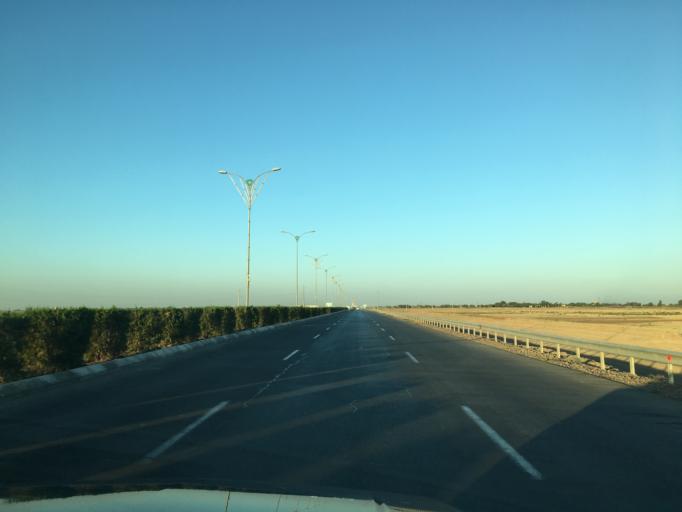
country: TM
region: Dasoguz
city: Dasoguz
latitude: 41.7804
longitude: 59.8545
